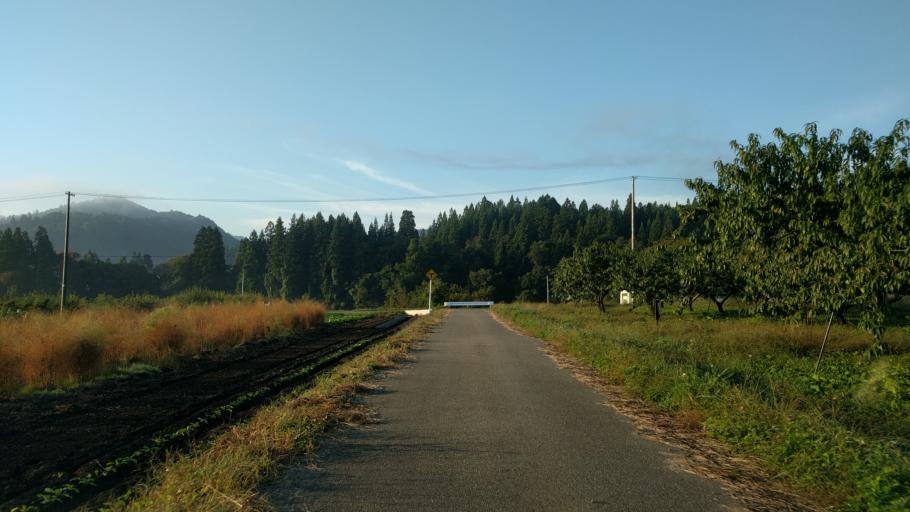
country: JP
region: Fukushima
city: Kitakata
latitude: 37.4338
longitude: 139.8006
